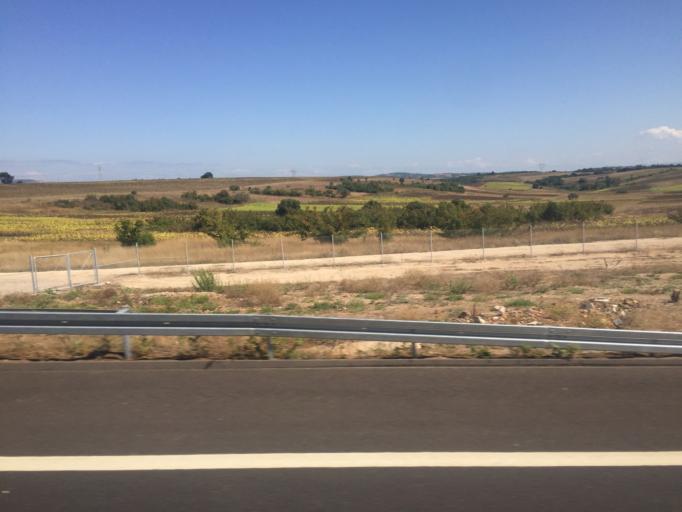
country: TR
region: Bursa
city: Mahmudiye
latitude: 40.2707
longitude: 28.6190
